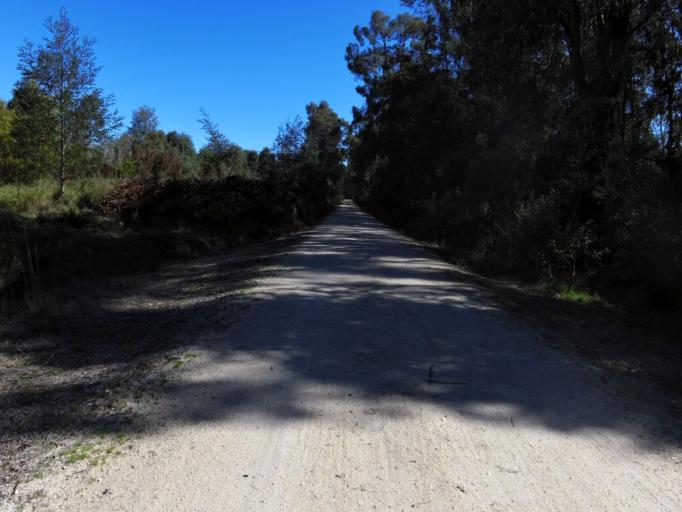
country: AU
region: Victoria
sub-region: Latrobe
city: Moe
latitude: -38.3739
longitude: 146.1999
